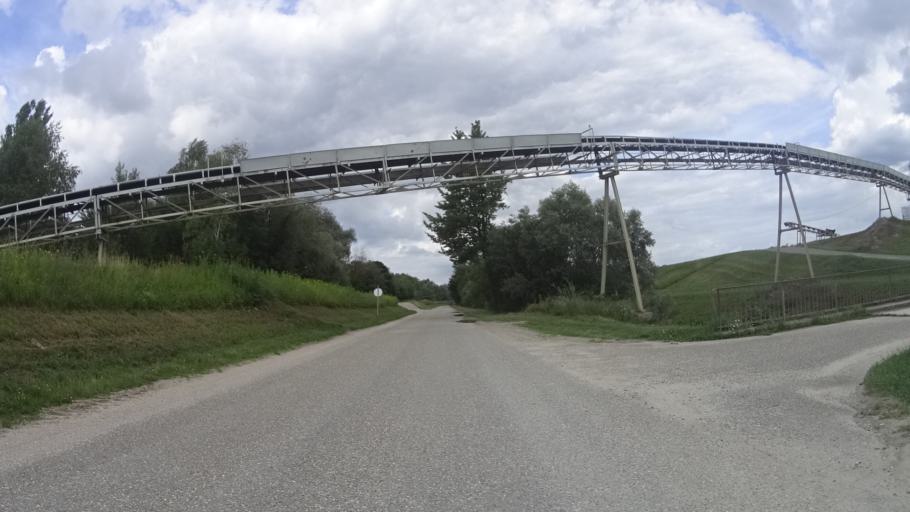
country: DE
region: Baden-Wuerttemberg
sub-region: Karlsruhe Region
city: Rheinmuenster
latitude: 48.7901
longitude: 8.0290
